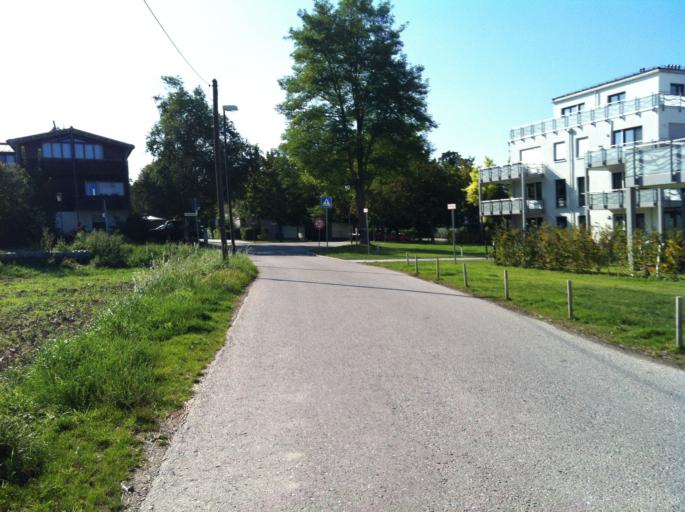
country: DE
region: Bavaria
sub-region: Upper Bavaria
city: Garching bei Munchen
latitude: 48.2499
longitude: 11.6580
